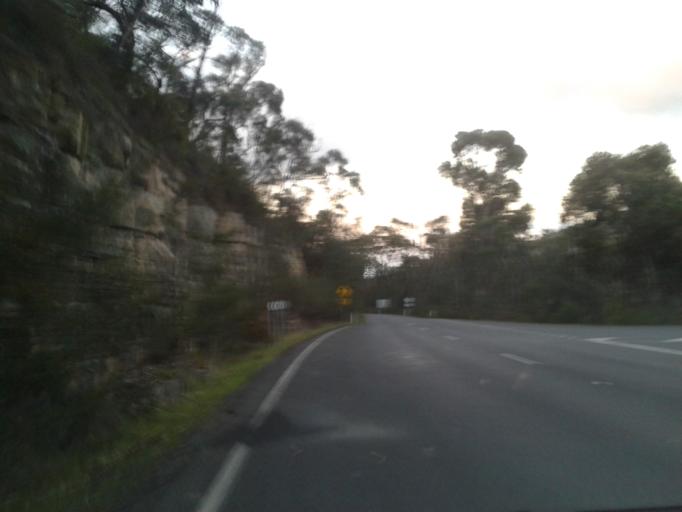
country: AU
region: Victoria
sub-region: Northern Grampians
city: Stawell
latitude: -37.1589
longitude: 142.4971
